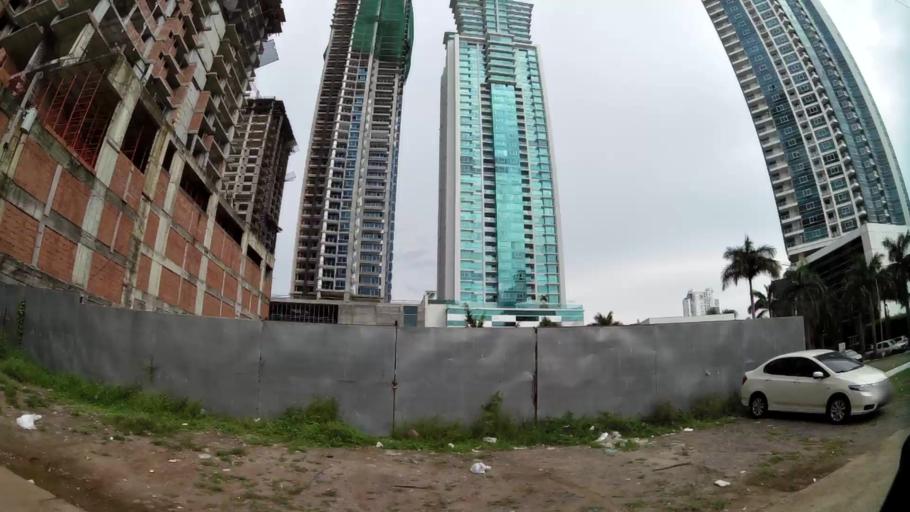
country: PA
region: Panama
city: San Miguelito
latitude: 9.0104
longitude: -79.4705
